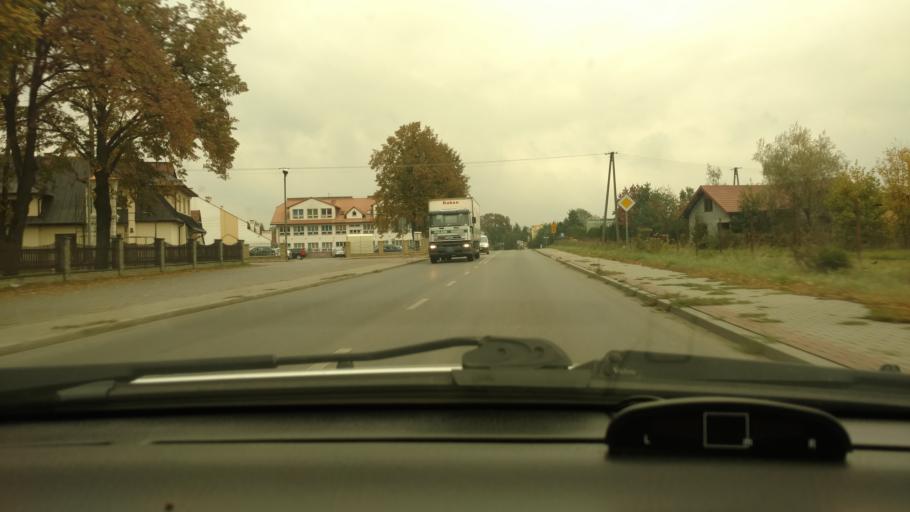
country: PL
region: Lesser Poland Voivodeship
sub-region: Powiat nowosadecki
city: Chelmiec
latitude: 49.6047
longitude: 20.6504
